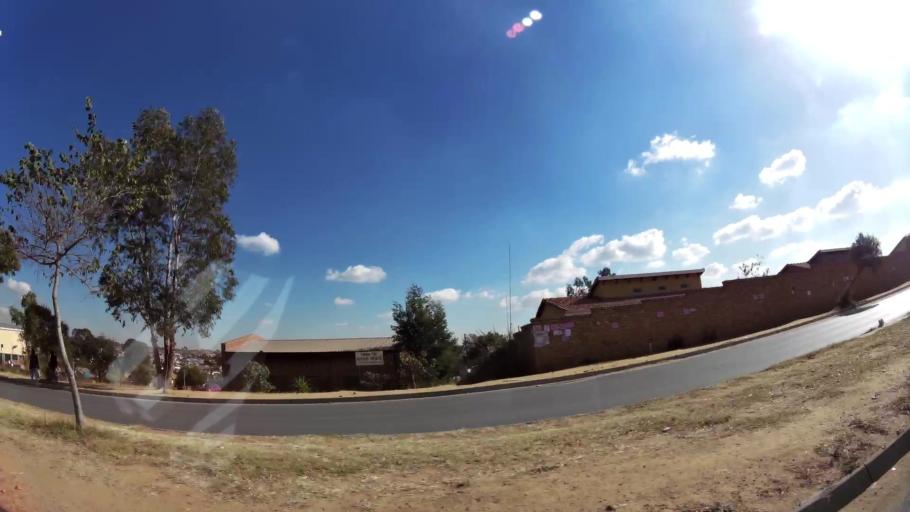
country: ZA
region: Gauteng
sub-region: West Rand District Municipality
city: Muldersdriseloop
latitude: -26.0190
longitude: 27.9351
